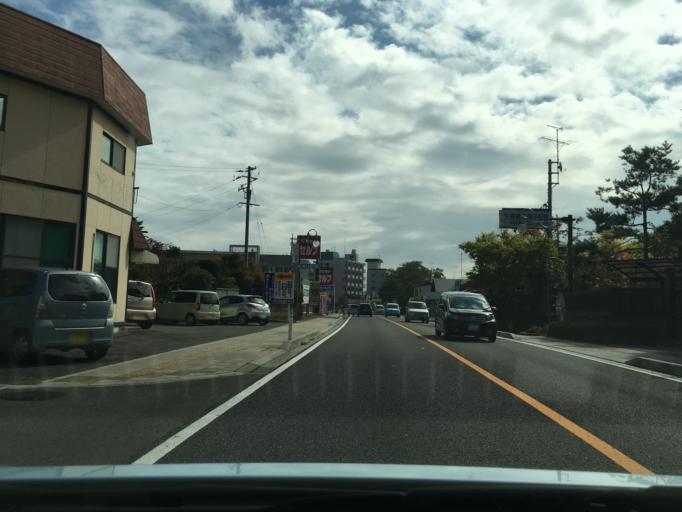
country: JP
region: Fukushima
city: Koriyama
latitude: 37.3818
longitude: 140.3636
